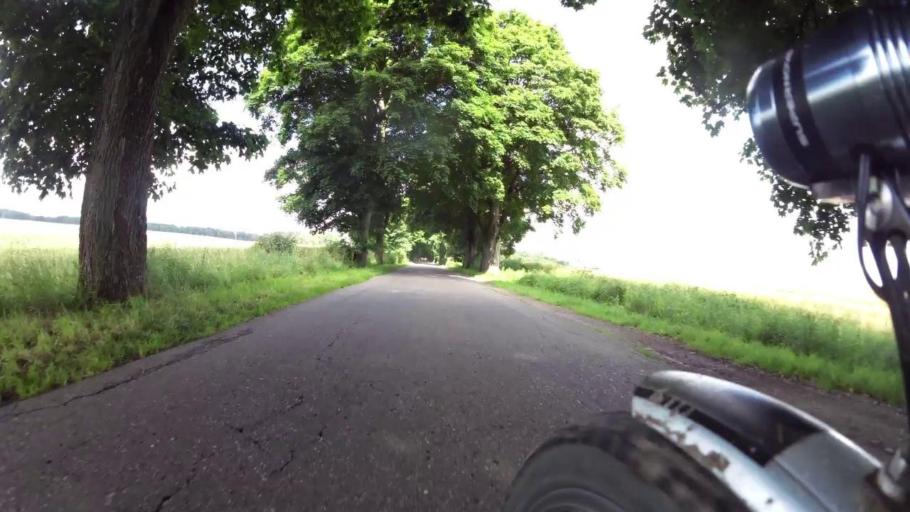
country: PL
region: West Pomeranian Voivodeship
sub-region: Powiat swidwinski
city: Rabino
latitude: 53.8079
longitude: 15.9088
